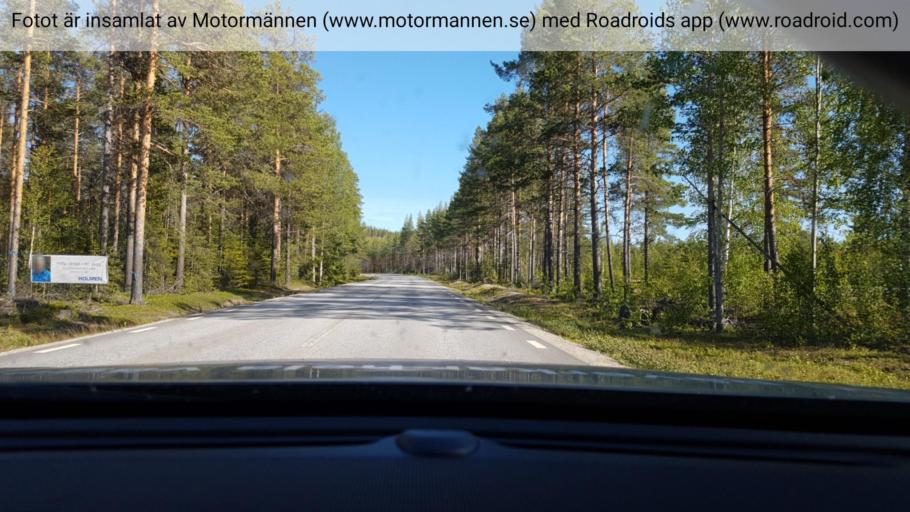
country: SE
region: Vaesterbotten
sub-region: Lycksele Kommun
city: Lycksele
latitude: 64.6307
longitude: 18.5761
